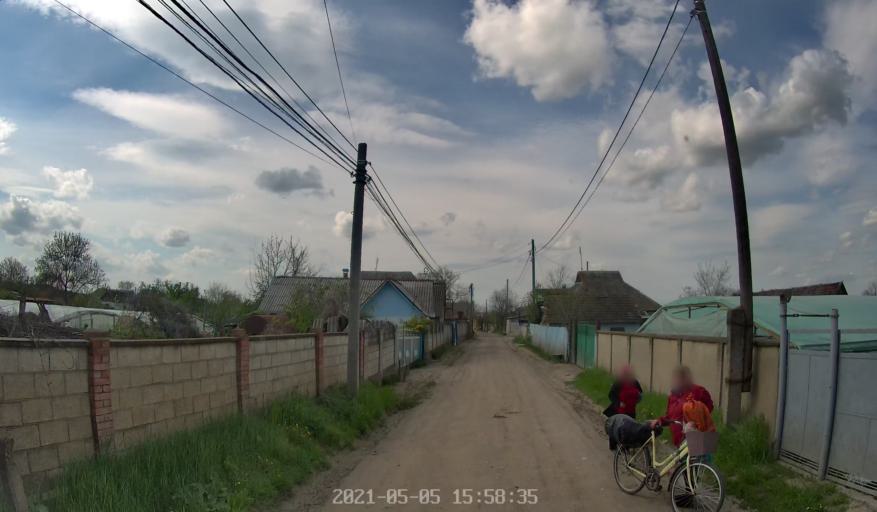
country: MD
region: Criuleni
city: Criuleni
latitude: 47.1385
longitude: 29.2036
